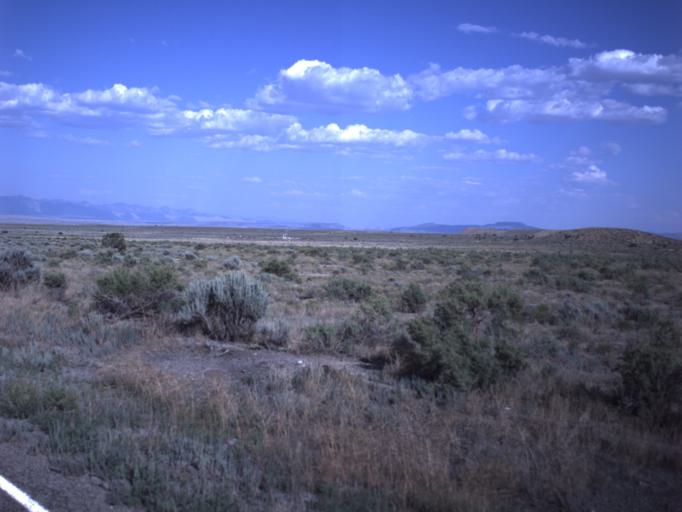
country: US
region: Utah
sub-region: Carbon County
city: Price
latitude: 39.4843
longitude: -110.8879
